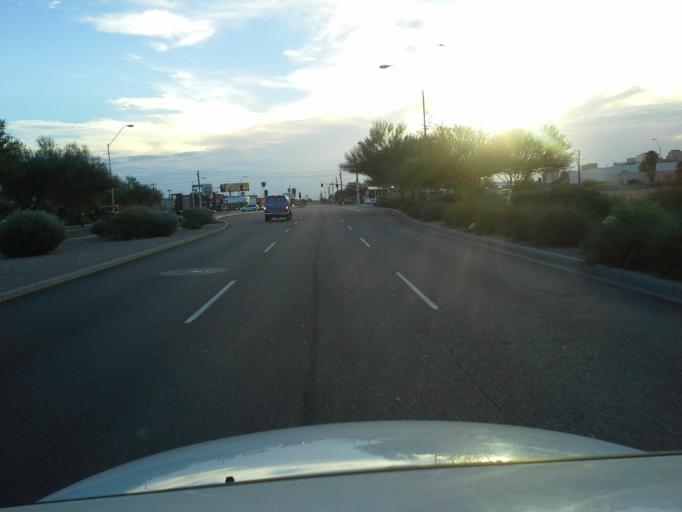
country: US
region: Arizona
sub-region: Maricopa County
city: Phoenix
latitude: 33.4370
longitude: -112.0458
